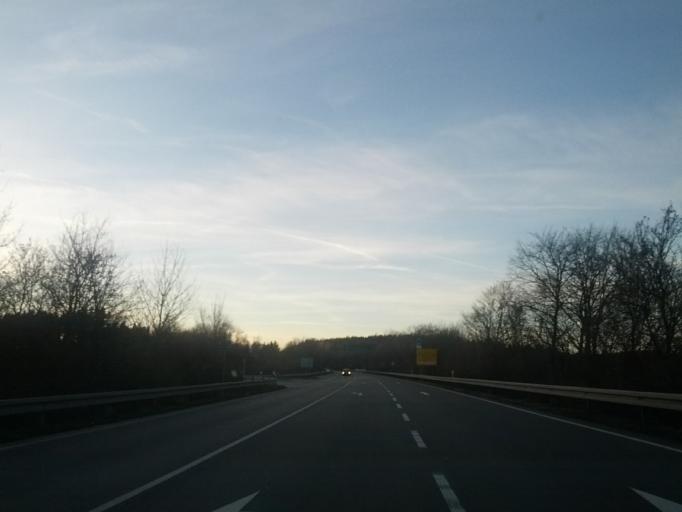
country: DE
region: Baden-Wuerttemberg
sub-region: Tuebingen Region
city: Berkheim
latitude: 48.0494
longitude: 10.0837
